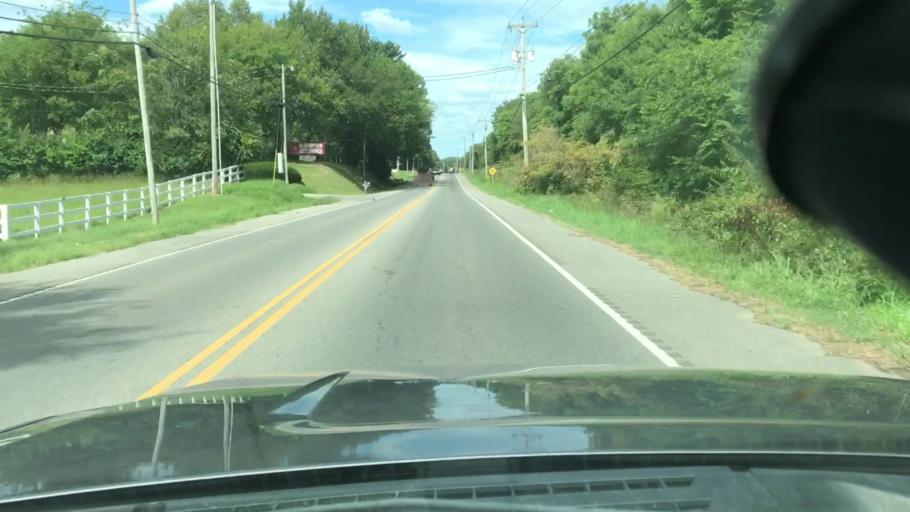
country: US
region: Tennessee
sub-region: Williamson County
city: Franklin
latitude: 35.9534
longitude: -86.8464
